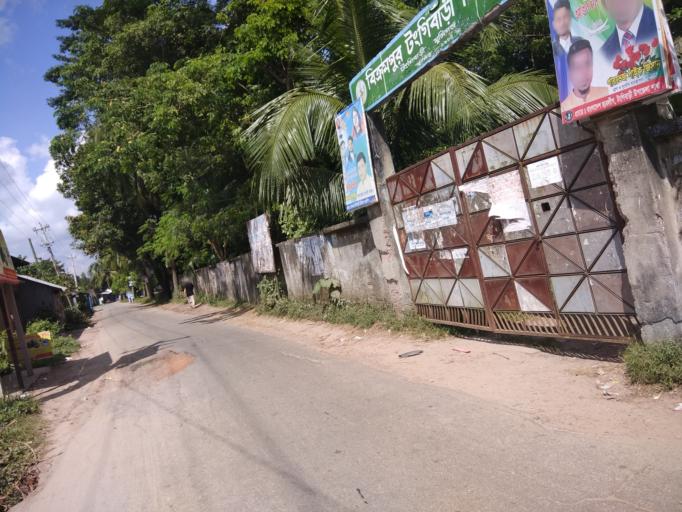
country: BD
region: Dhaka
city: Narayanganj
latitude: 23.5027
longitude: 90.4615
